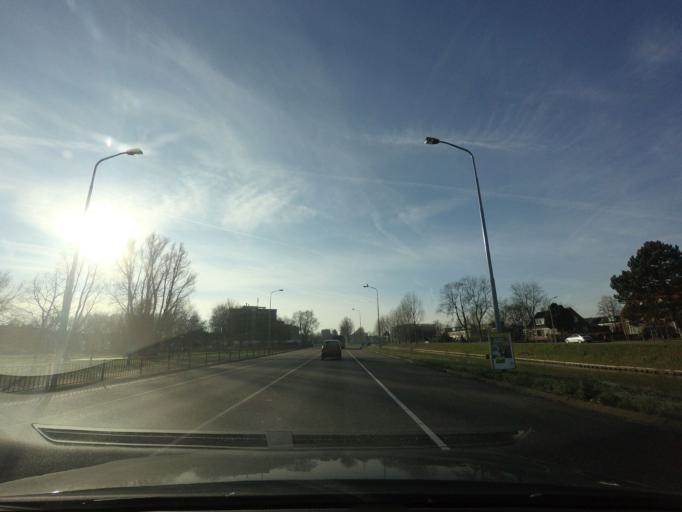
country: NL
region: North Holland
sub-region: Gemeente Haarlemmermeer
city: Hoofddorp
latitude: 52.2990
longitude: 4.6836
